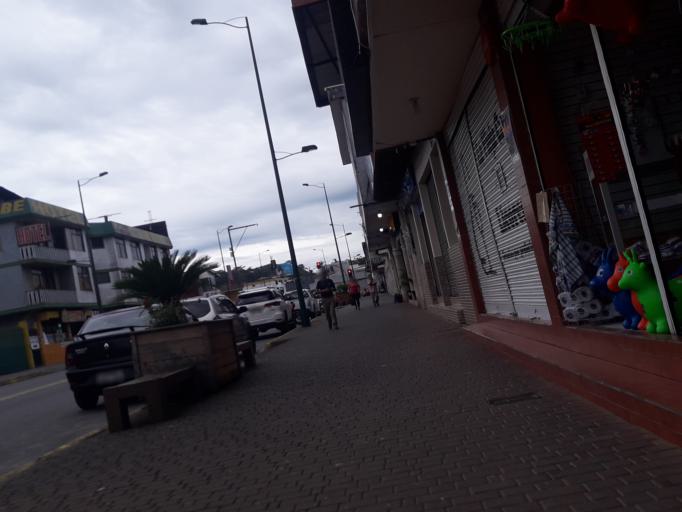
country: EC
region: Napo
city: Tena
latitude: -1.0024
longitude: -77.8114
